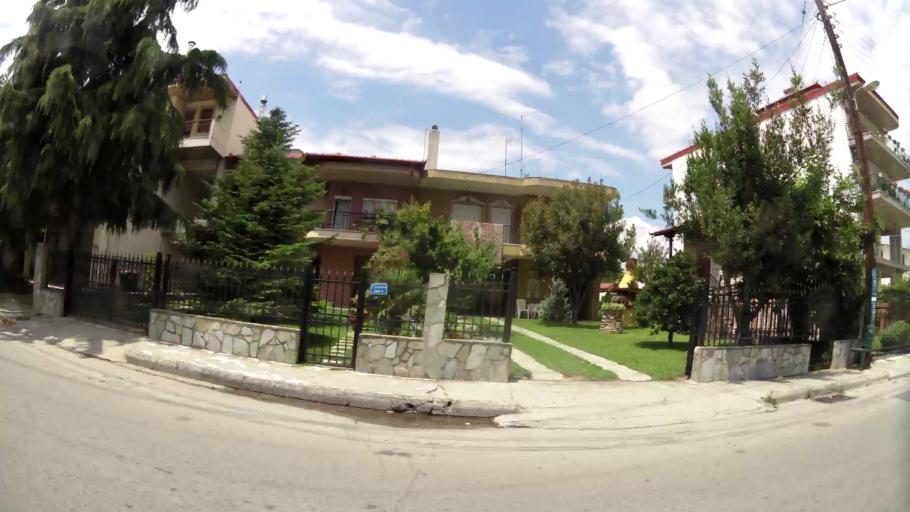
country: GR
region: Central Macedonia
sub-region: Nomos Pierias
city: Katerini
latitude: 40.2626
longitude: 22.5086
